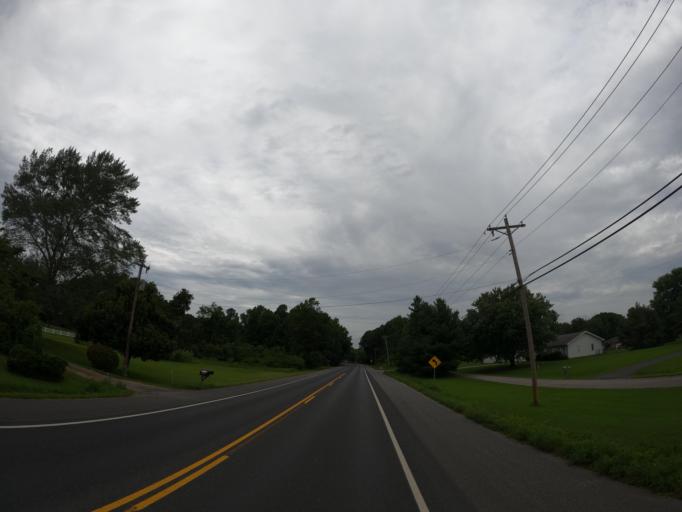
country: US
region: Maryland
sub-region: Saint Mary's County
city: California
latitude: 38.2284
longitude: -76.5191
